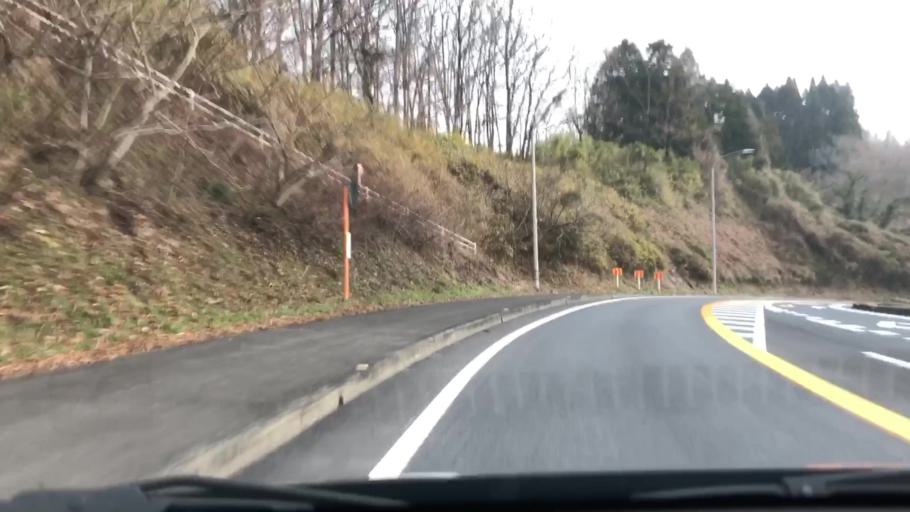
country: JP
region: Oita
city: Takedamachi
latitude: 32.9732
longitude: 131.5196
